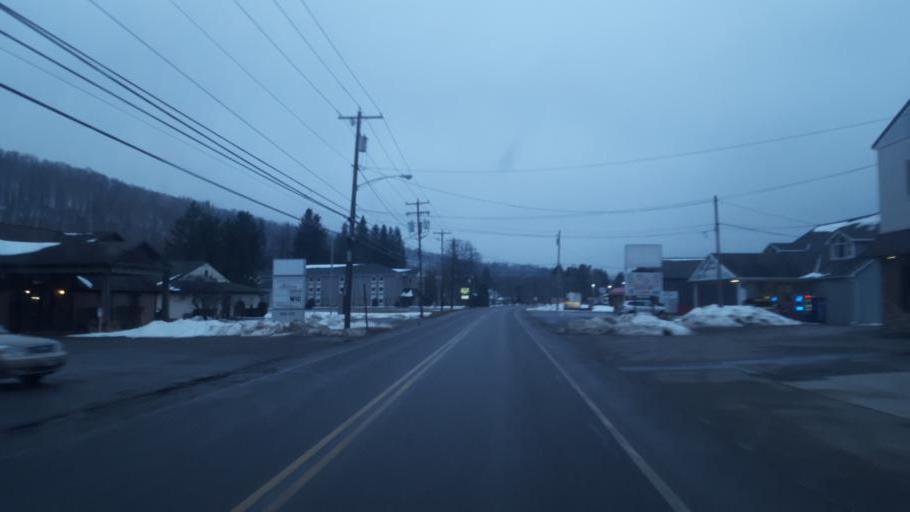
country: US
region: Pennsylvania
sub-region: Potter County
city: Coudersport
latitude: 41.7655
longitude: -78.0322
